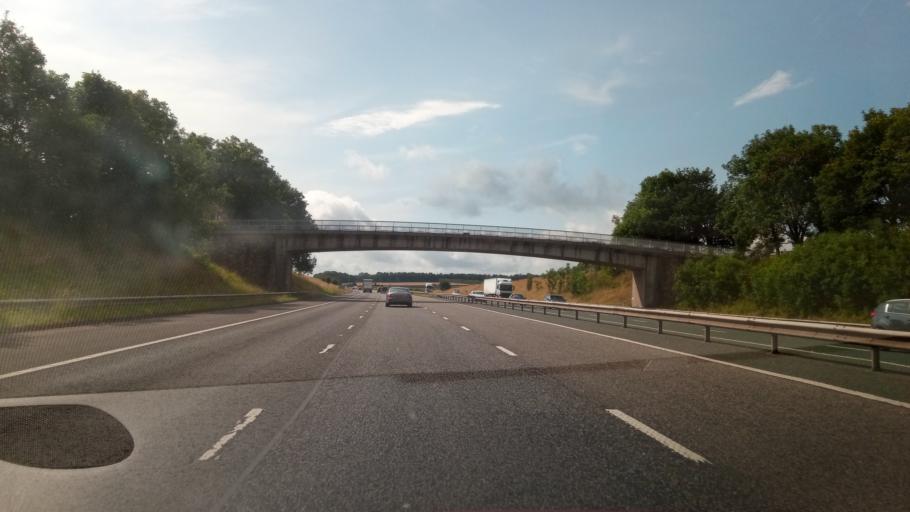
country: GB
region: England
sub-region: Cumbria
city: Penrith
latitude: 54.6237
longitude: -2.7219
